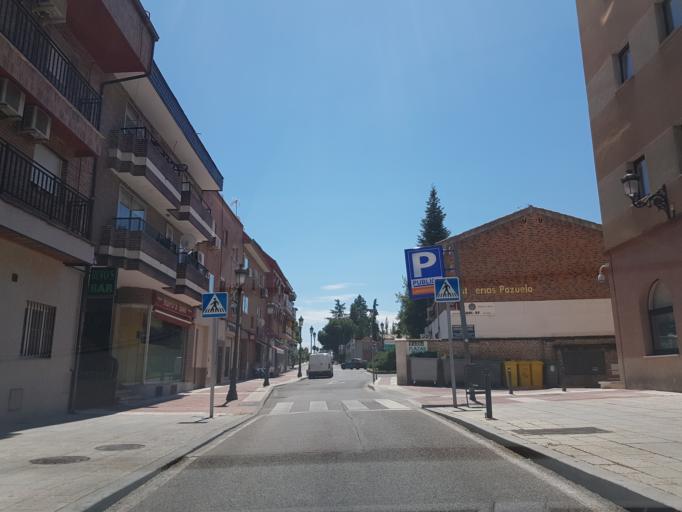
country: ES
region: Madrid
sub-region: Provincia de Madrid
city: Pozuelo de Alarcon
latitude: 40.4345
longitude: -3.8136
